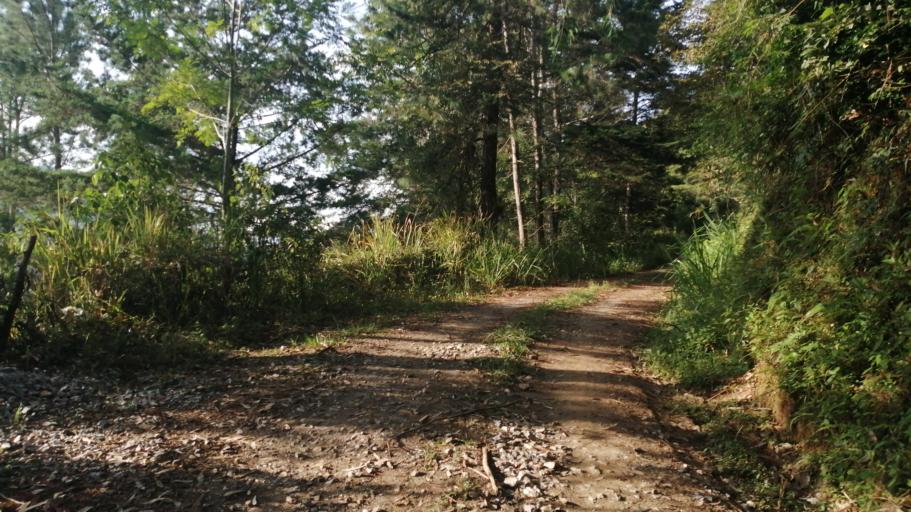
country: CO
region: Boyaca
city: Garagoa
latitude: 5.0787
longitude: -73.3886
